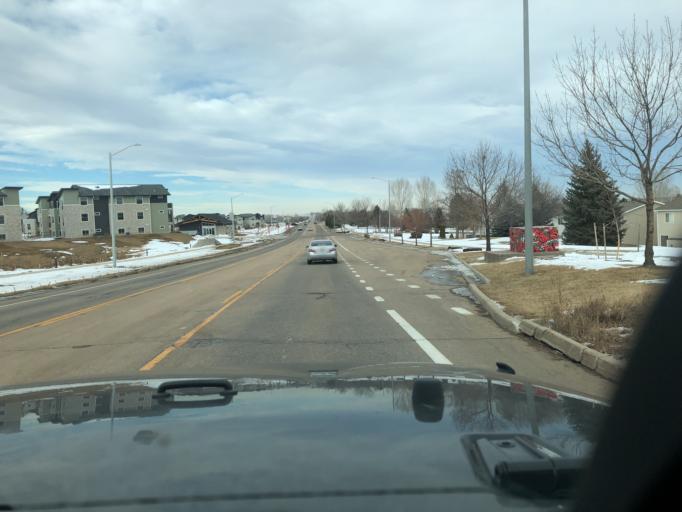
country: US
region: Colorado
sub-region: Boulder County
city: Longmont
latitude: 40.1769
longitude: -105.0741
